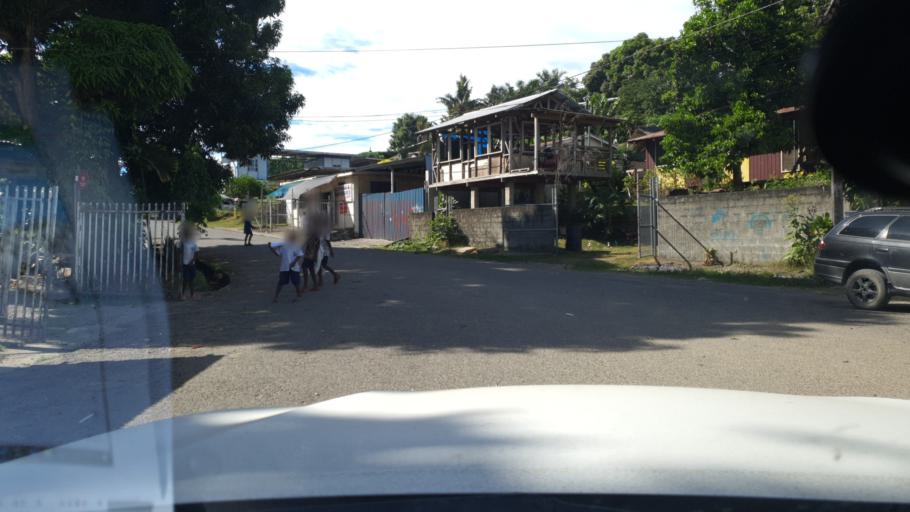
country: SB
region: Guadalcanal
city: Honiara
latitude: -9.4387
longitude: 159.9577
